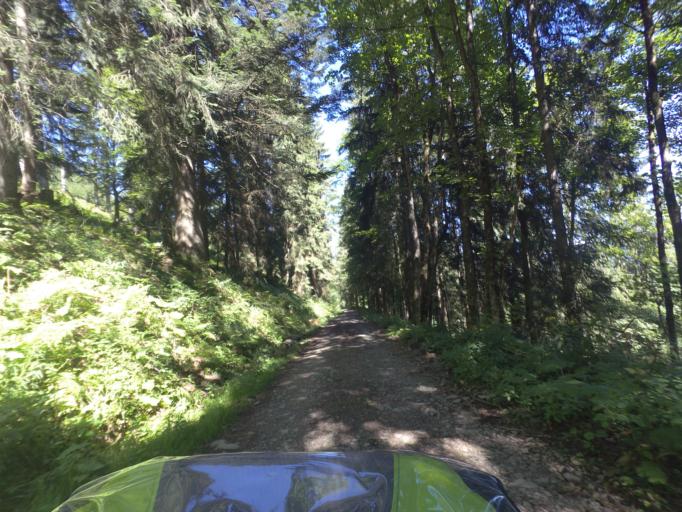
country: AT
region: Salzburg
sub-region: Politischer Bezirk Hallein
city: Hallein
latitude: 47.6396
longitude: 13.1014
